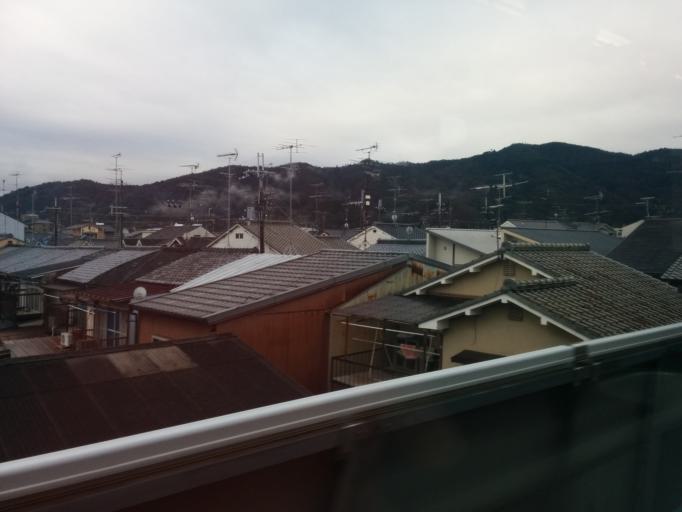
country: JP
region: Kyoto
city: Muko
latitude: 35.0181
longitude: 135.6881
